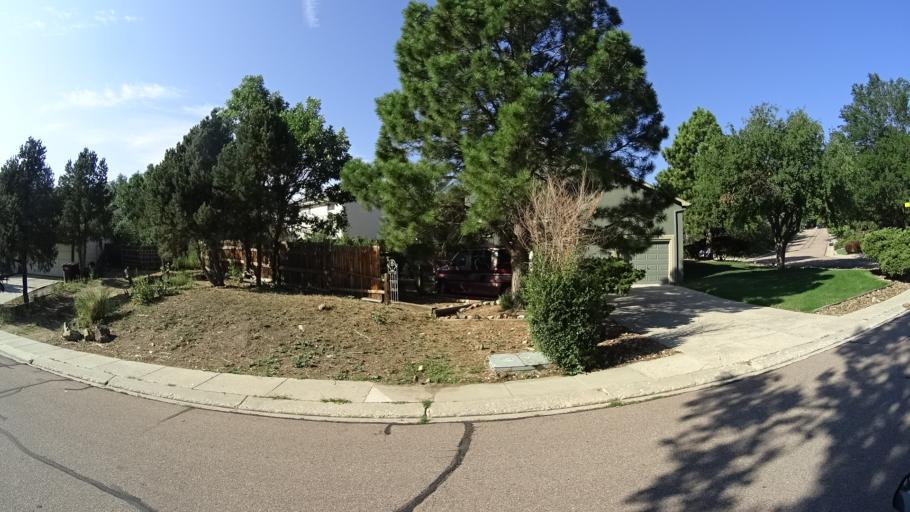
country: US
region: Colorado
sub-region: El Paso County
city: Colorado Springs
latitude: 38.8837
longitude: -104.8421
